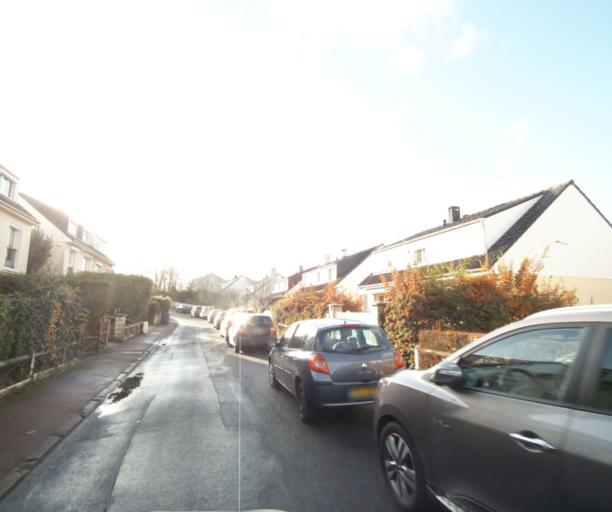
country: FR
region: Ile-de-France
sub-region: Departement des Yvelines
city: Meulan-en-Yvelines
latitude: 49.0107
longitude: 1.9130
